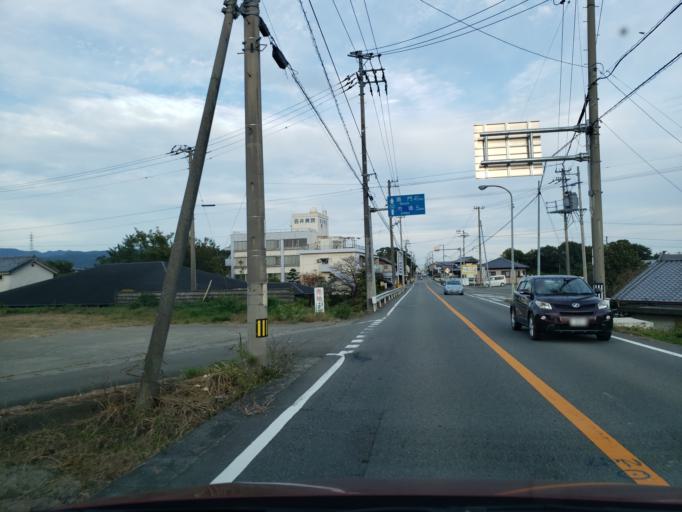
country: JP
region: Tokushima
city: Wakimachi
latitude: 34.0758
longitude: 134.2384
